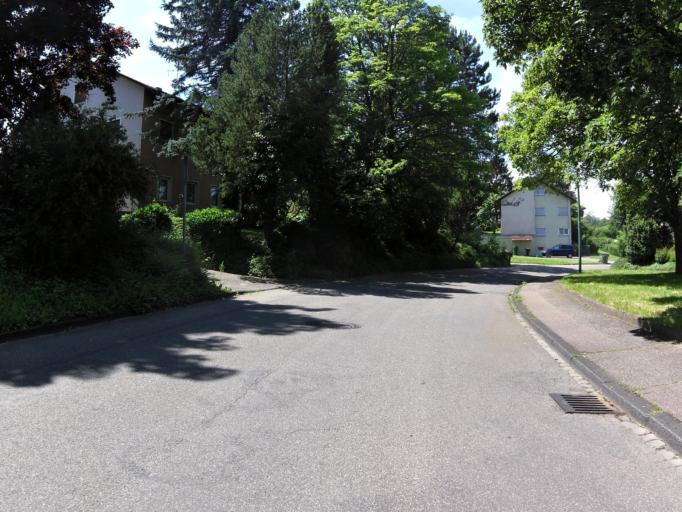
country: DE
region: Baden-Wuerttemberg
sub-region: Freiburg Region
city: Lahr
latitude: 48.3281
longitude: 7.8661
